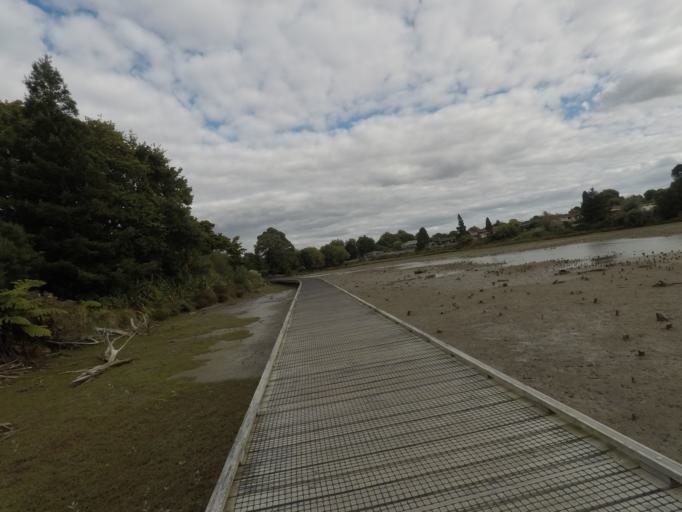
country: NZ
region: Auckland
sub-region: Auckland
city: Papakura
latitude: -37.0636
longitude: 174.9331
